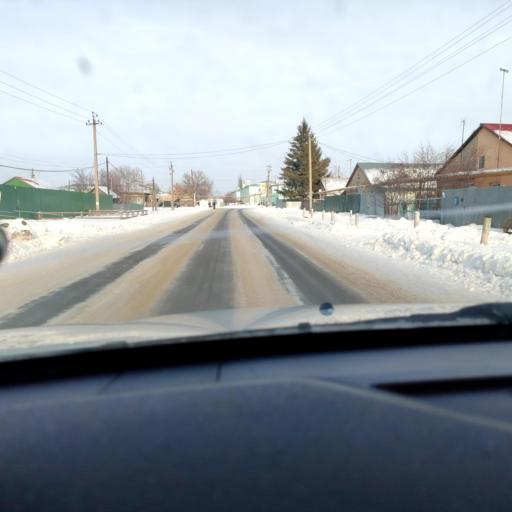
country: RU
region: Samara
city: Smyshlyayevka
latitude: 53.1625
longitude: 50.3827
